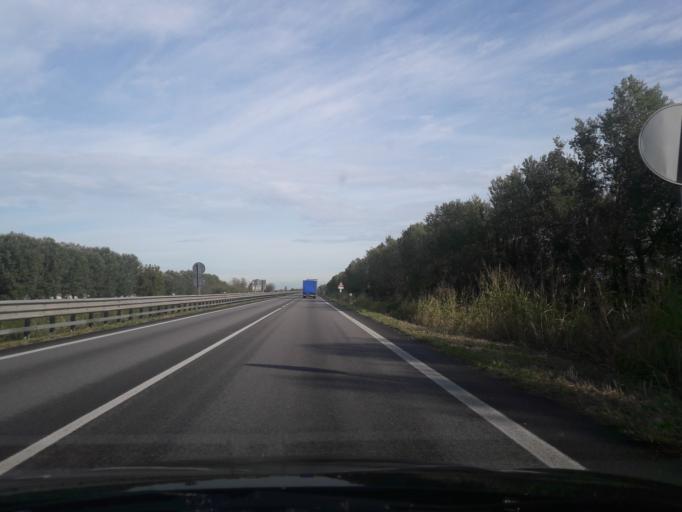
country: IT
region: Veneto
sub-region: Provincia di Venezia
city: Campagna Lupia
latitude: 45.3685
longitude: 12.1380
